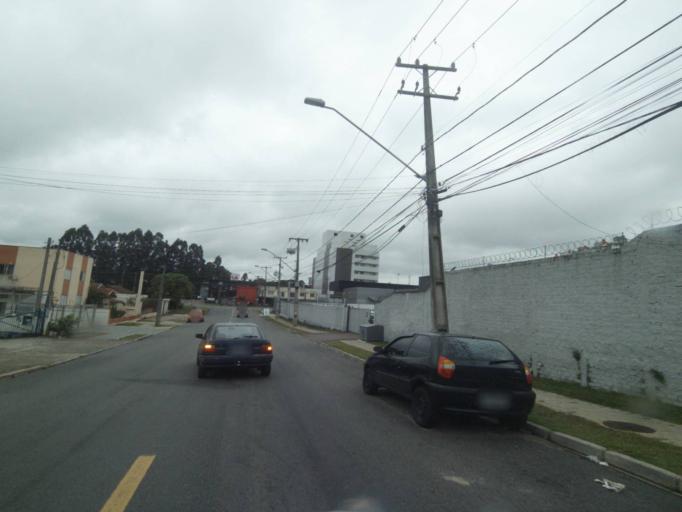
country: BR
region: Parana
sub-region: Curitiba
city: Curitiba
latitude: -25.4345
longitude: -49.3116
